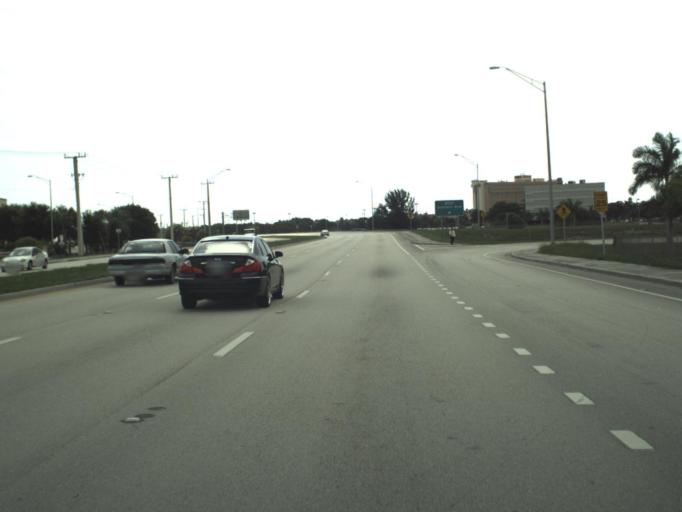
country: US
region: Florida
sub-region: Palm Beach County
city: Lake Clarke Shores
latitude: 26.6777
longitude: -80.0793
